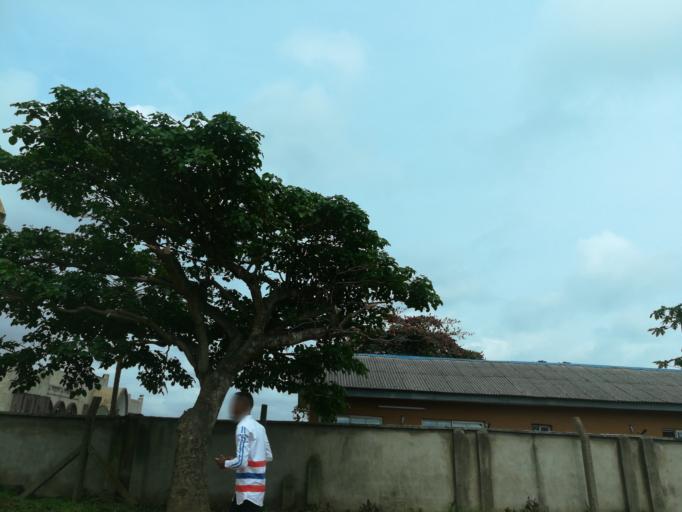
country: NG
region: Lagos
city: Oshodi
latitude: 6.5734
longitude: 3.3235
